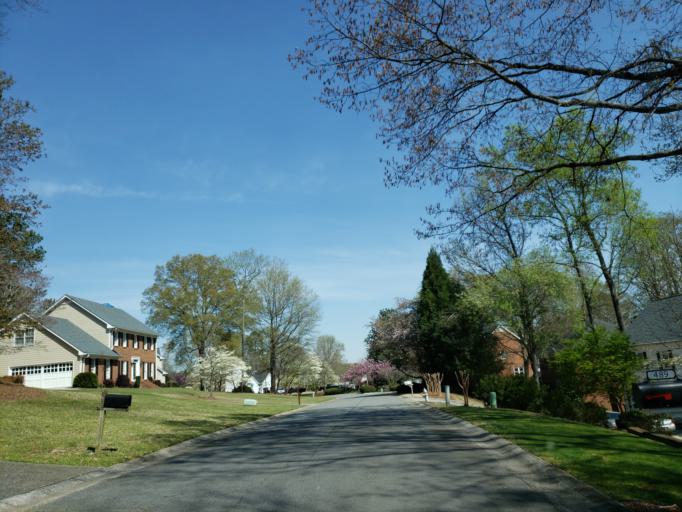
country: US
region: Georgia
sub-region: Cobb County
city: Marietta
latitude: 33.9731
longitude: -84.5689
